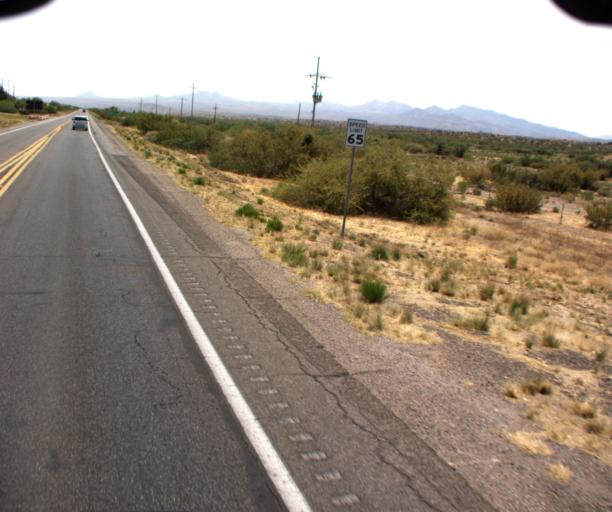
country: US
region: Arizona
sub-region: Gila County
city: Globe
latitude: 33.3729
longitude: -110.7367
